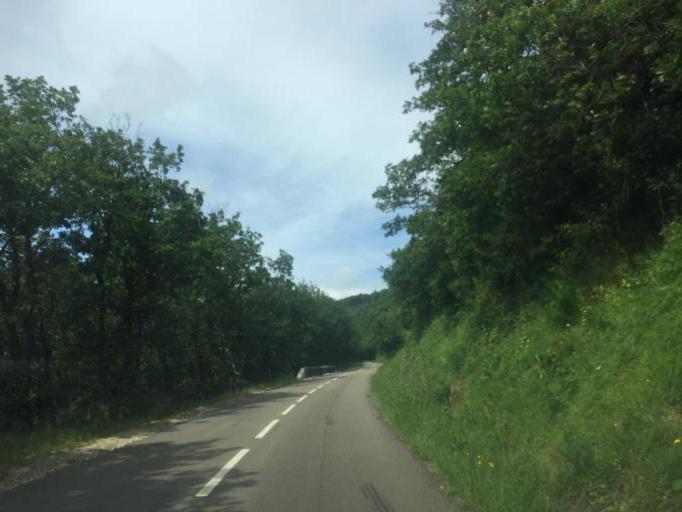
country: FR
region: Rhone-Alpes
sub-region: Departement de l'Ardeche
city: Villeneuve-de-Berg
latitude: 44.6273
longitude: 4.5452
